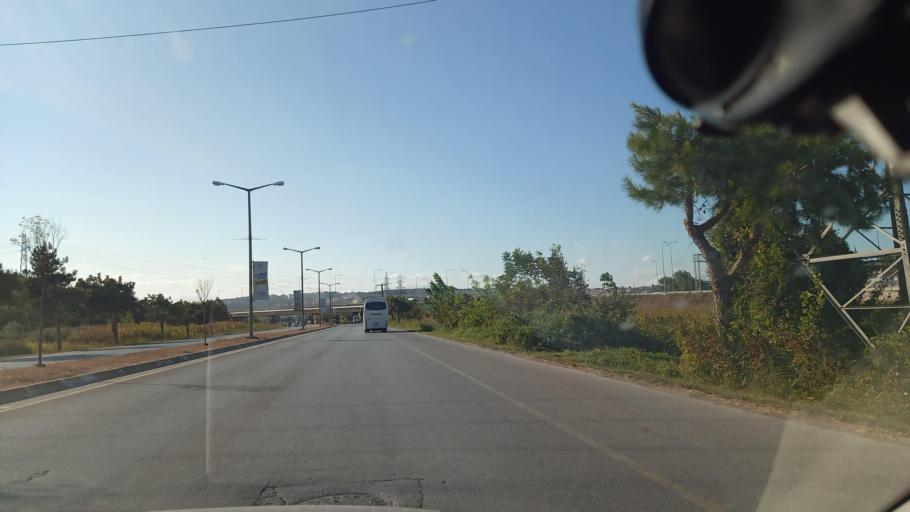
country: TR
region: Sakarya
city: Kazimpasa
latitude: 40.8425
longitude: 30.3360
